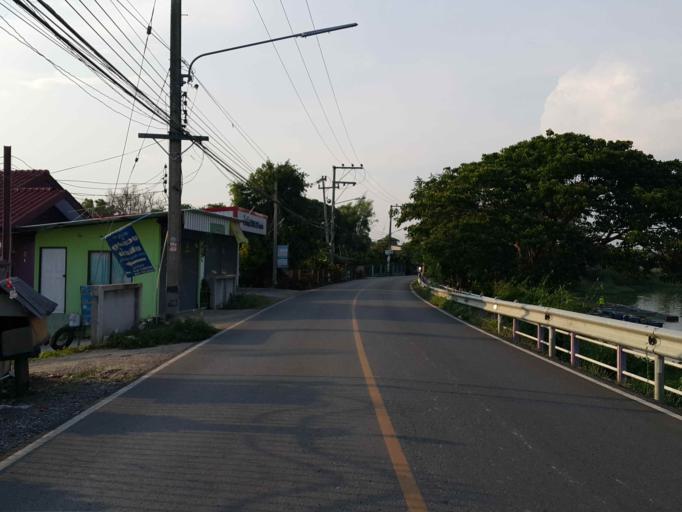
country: TH
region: Chiang Mai
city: Saraphi
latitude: 18.7087
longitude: 98.9825
